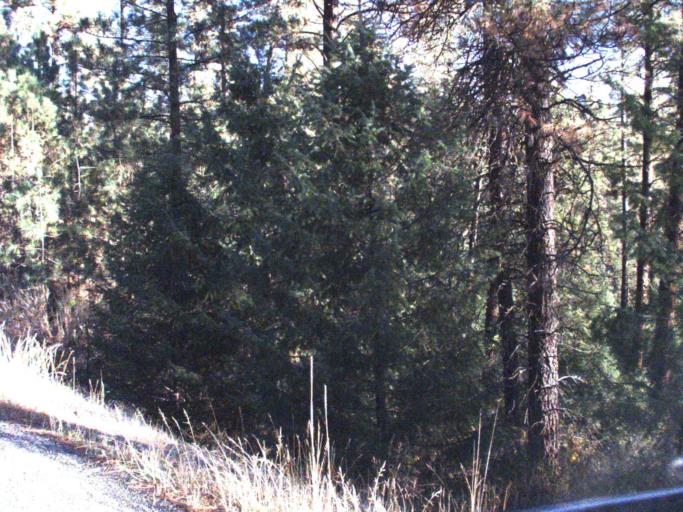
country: US
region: Washington
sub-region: Okanogan County
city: Coulee Dam
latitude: 48.0595
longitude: -118.6728
